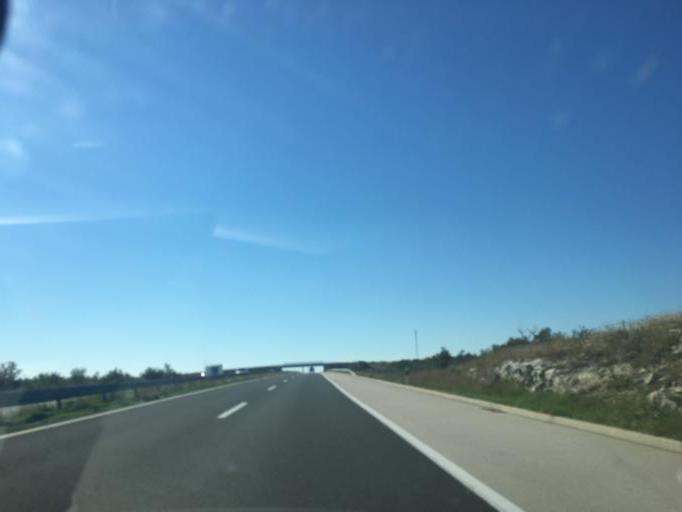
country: HR
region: Zadarska
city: Policnik
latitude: 44.1459
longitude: 15.4206
